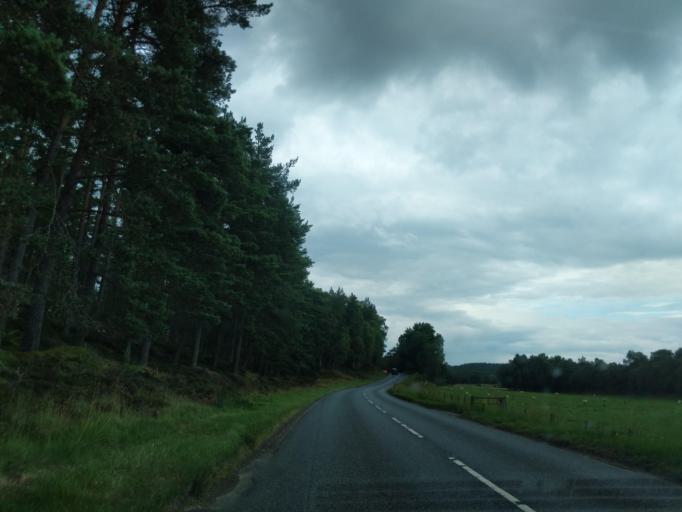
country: GB
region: Scotland
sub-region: Highland
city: Aviemore
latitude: 57.2928
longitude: -3.7909
